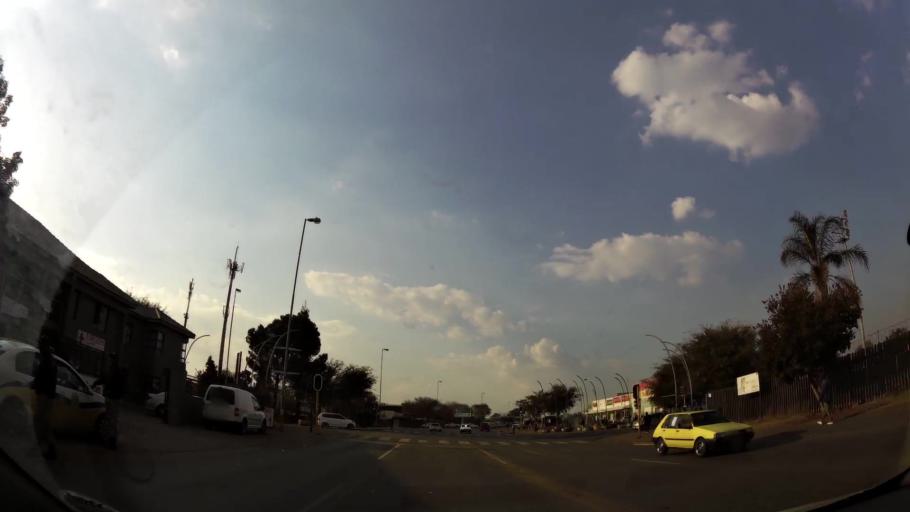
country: ZA
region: Gauteng
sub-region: Ekurhuleni Metropolitan Municipality
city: Germiston
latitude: -26.3511
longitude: 28.1993
